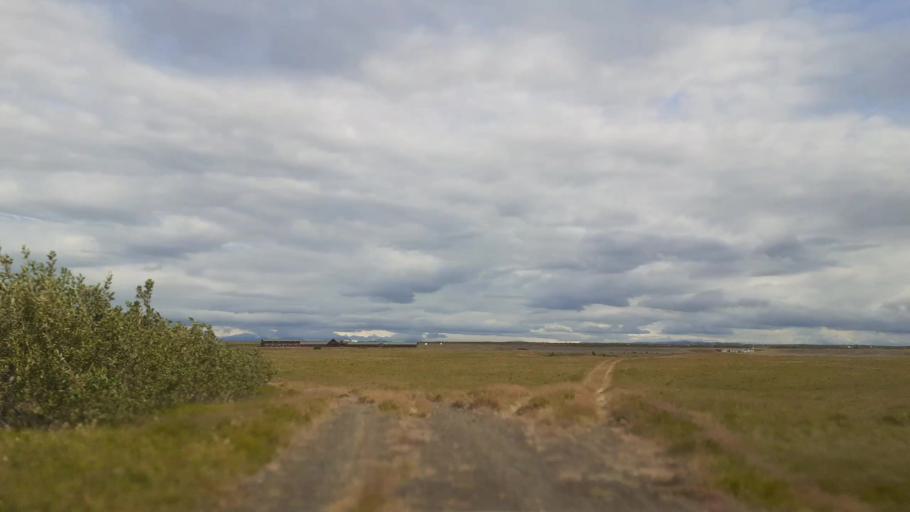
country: IS
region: South
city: Vestmannaeyjar
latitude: 63.7735
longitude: -20.2987
